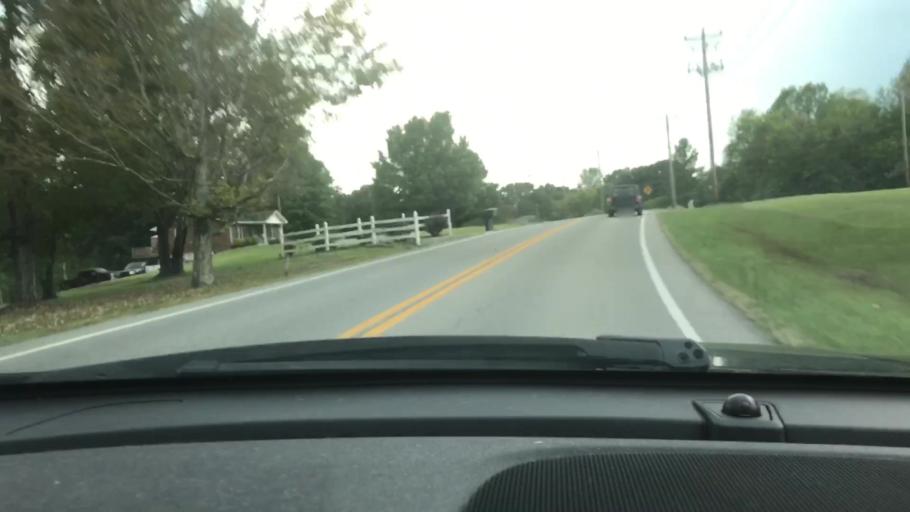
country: US
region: Tennessee
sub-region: Dickson County
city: Charlotte
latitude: 36.2433
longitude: -87.2431
